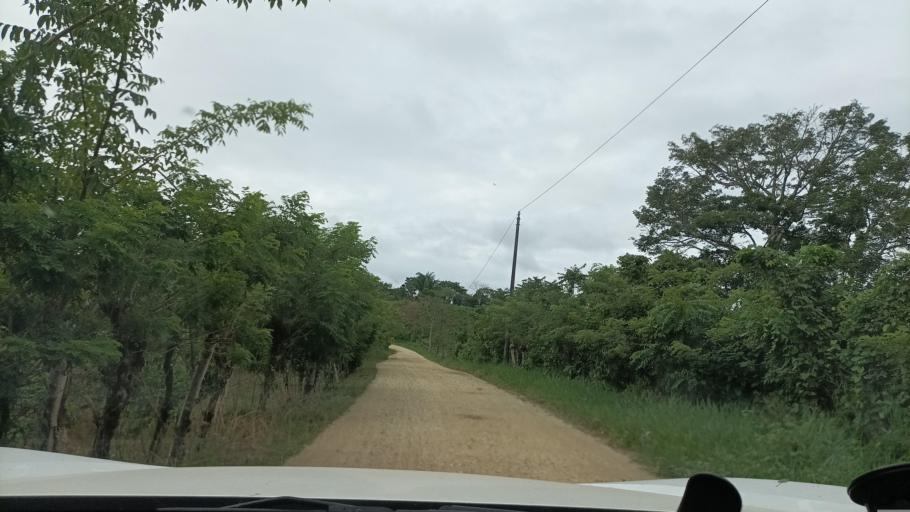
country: MX
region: Veracruz
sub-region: Uxpanapa
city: Poblado 10
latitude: 17.5602
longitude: -94.4256
